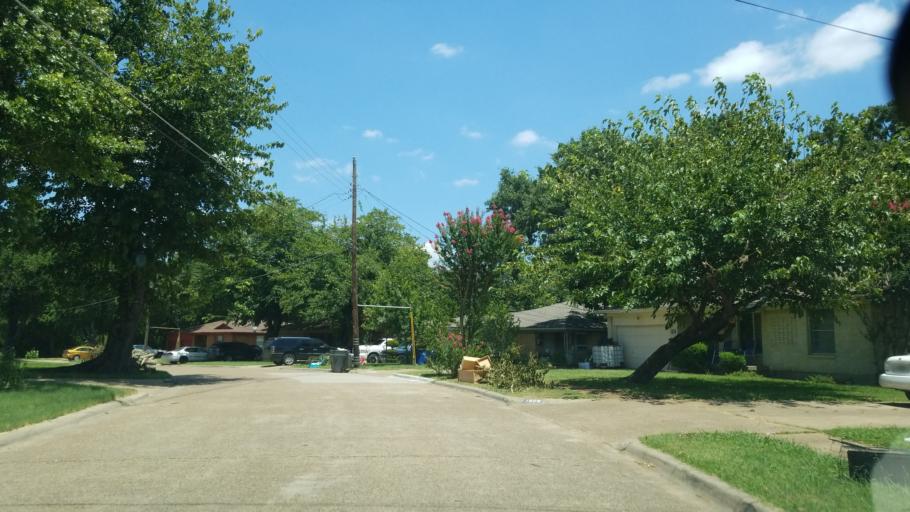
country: US
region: Texas
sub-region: Dallas County
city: Balch Springs
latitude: 32.7384
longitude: -96.7094
